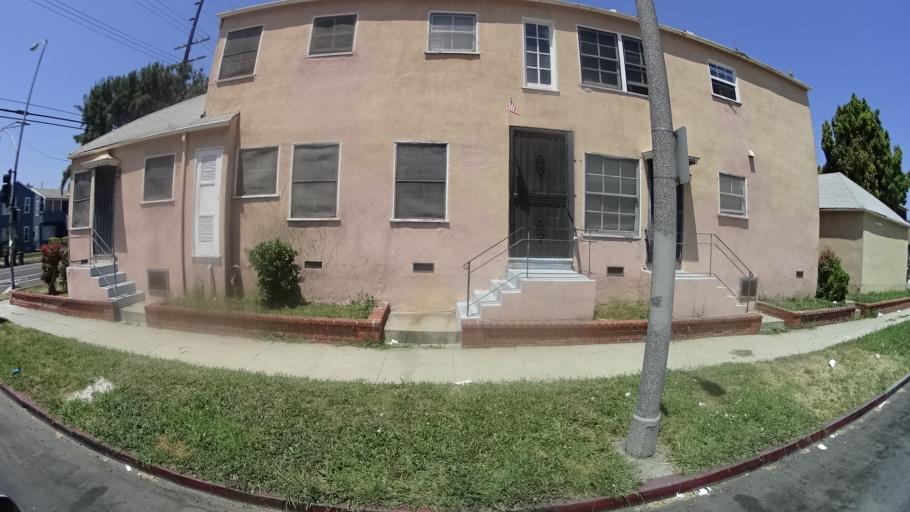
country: US
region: California
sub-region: Los Angeles County
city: View Park-Windsor Hills
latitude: 34.0003
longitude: -118.3215
